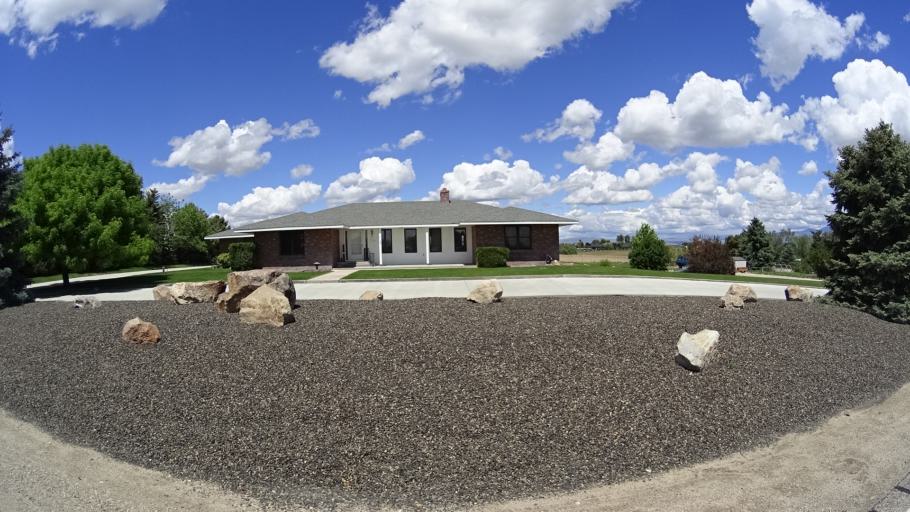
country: US
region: Idaho
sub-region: Ada County
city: Meridian
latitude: 43.5830
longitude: -116.4395
